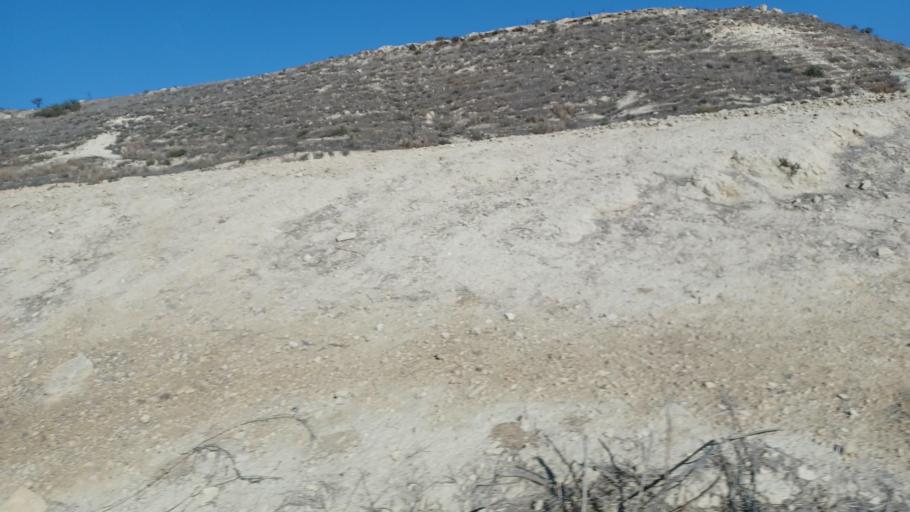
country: CY
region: Larnaka
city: Athienou
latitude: 35.0378
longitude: 33.5605
